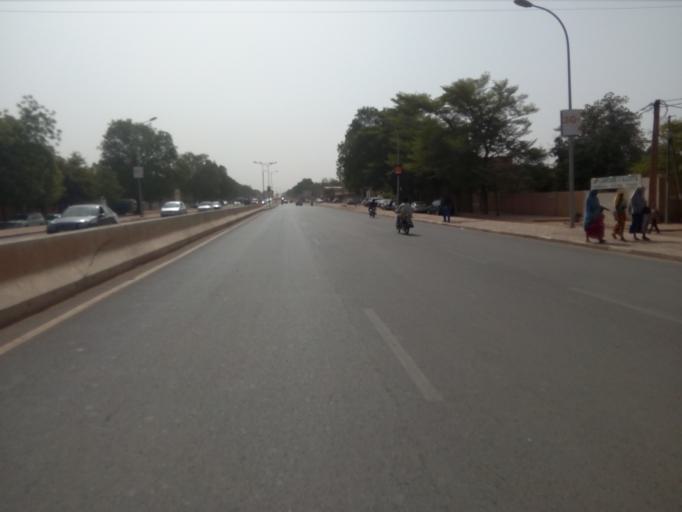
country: NE
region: Niamey
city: Niamey
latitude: 13.5342
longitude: 2.1056
